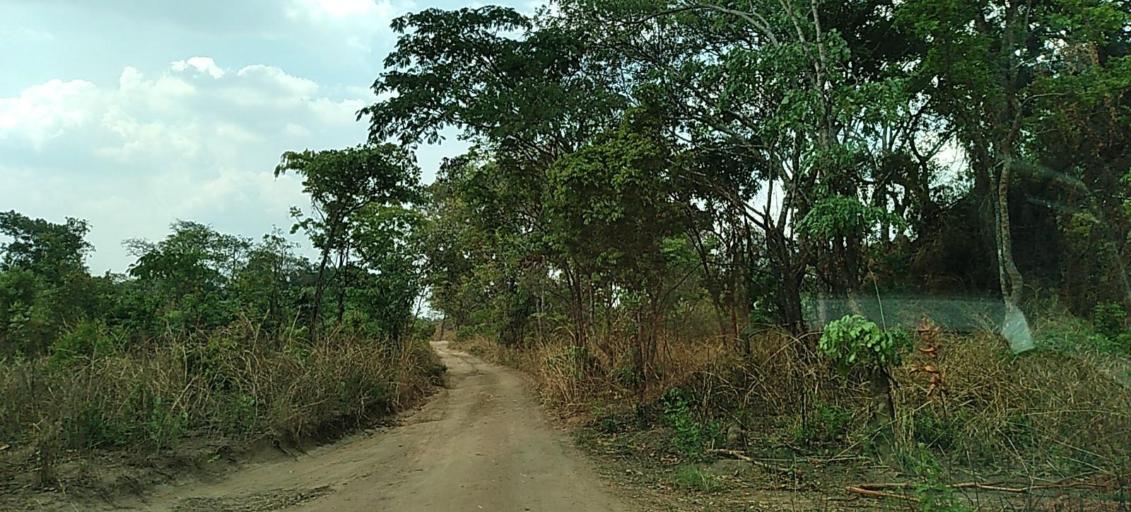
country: ZM
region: Copperbelt
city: Chililabombwe
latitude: -12.3285
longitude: 27.7483
